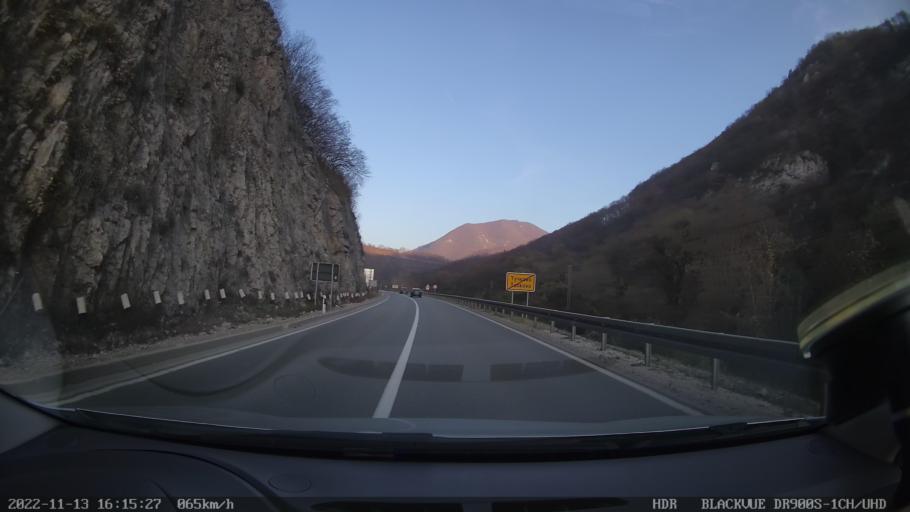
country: RS
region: Central Serbia
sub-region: Moravicki Okrug
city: Lucani
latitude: 43.8993
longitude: 20.1681
